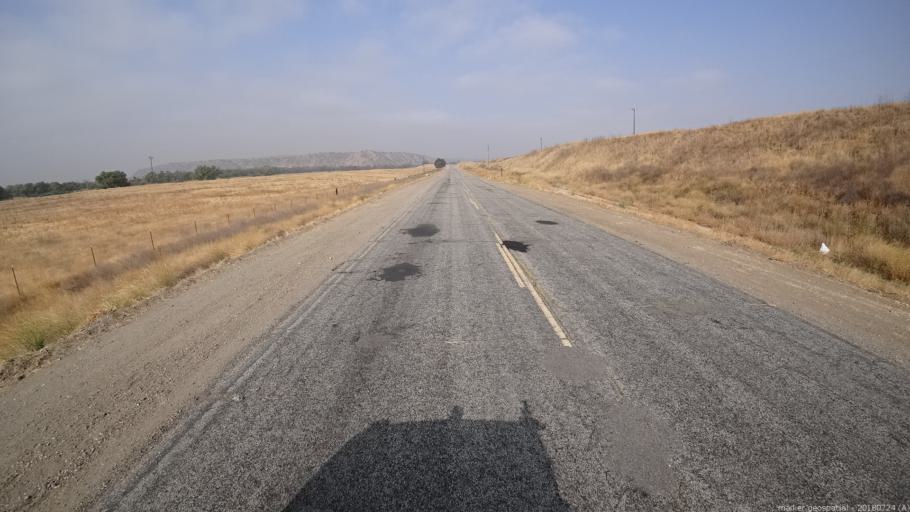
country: US
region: California
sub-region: San Luis Obispo County
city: San Miguel
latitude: 35.8621
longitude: -120.7832
